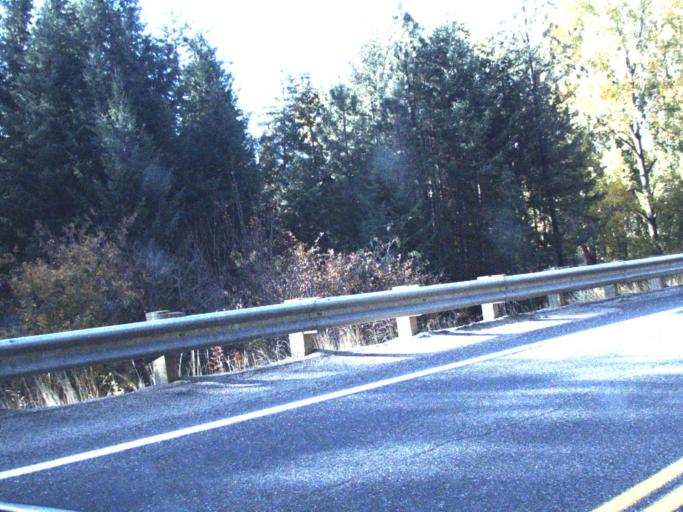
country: US
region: Washington
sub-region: Stevens County
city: Kettle Falls
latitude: 48.4819
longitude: -118.1733
